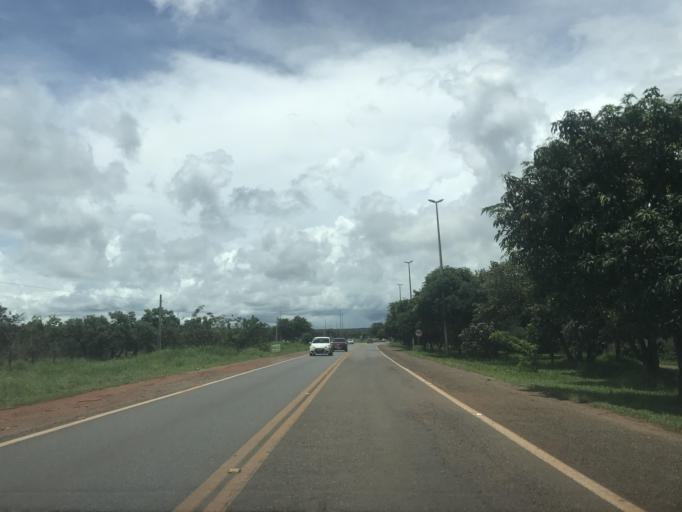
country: BR
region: Federal District
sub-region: Brasilia
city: Brasilia
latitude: -15.6905
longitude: -47.8319
